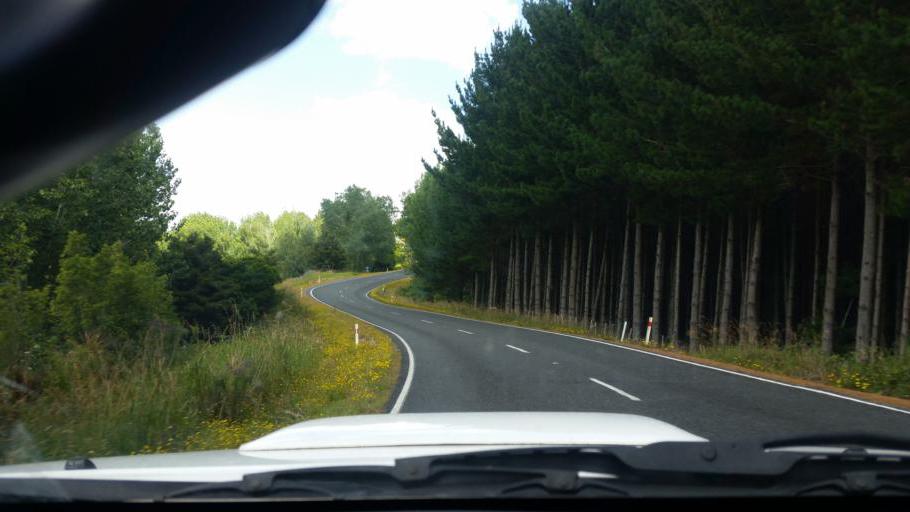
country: NZ
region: Northland
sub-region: Whangarei
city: Ruakaka
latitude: -36.0486
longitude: 174.2753
